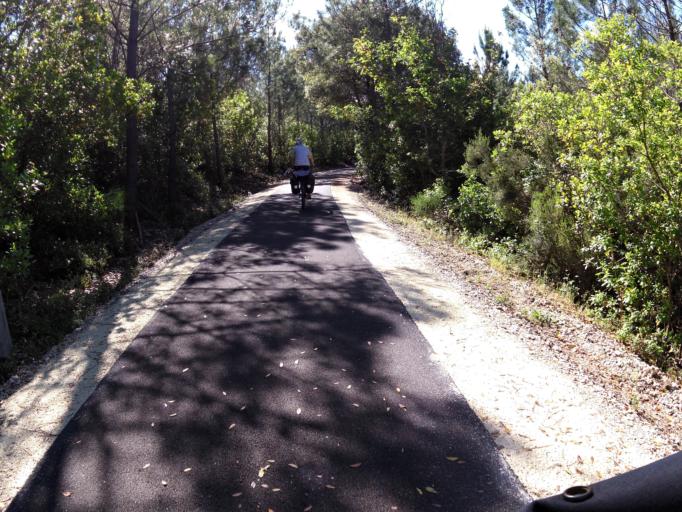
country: FR
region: Aquitaine
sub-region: Departement de la Gironde
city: Lacanau
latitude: 45.0319
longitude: -1.1771
